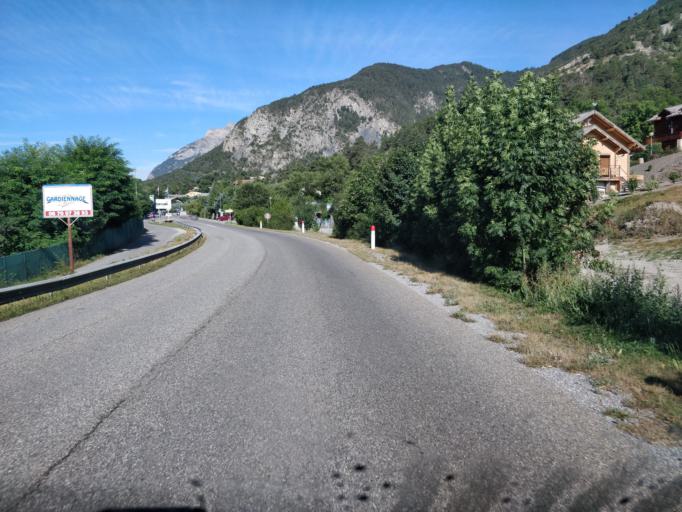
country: FR
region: Provence-Alpes-Cote d'Azur
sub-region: Departement des Alpes-de-Haute-Provence
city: Barcelonnette
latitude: 44.3928
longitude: 6.5759
